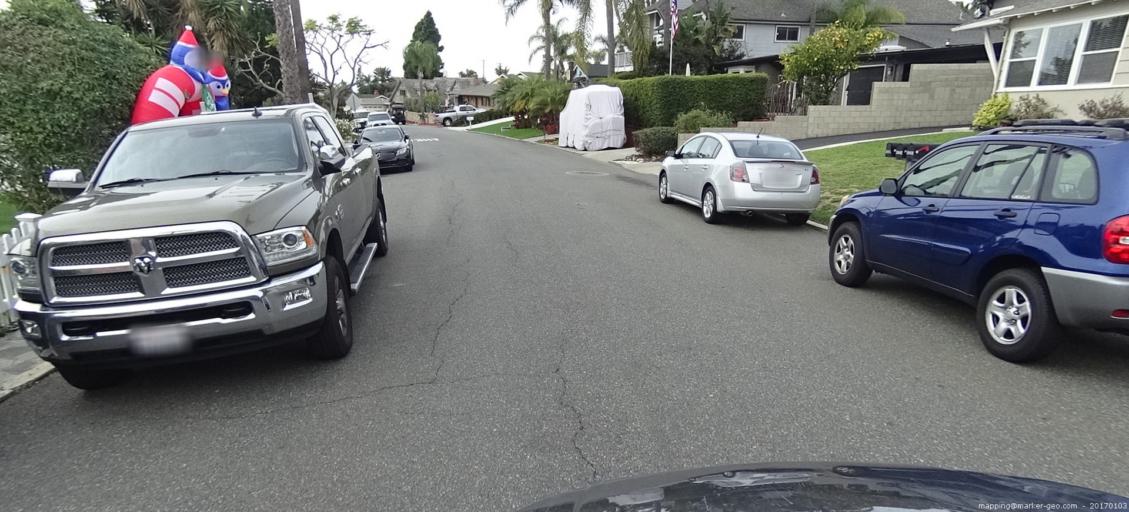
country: US
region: California
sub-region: Orange County
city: Dana Point
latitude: 33.4587
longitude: -117.6601
